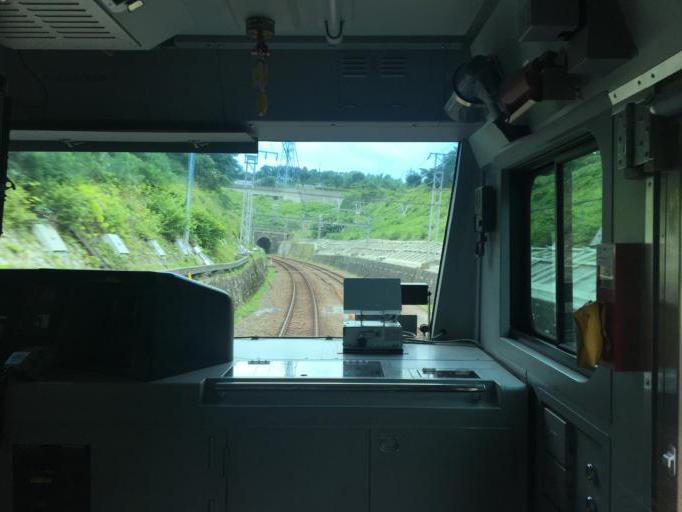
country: JP
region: Kanagawa
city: Yokohama
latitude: 35.4394
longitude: 139.5626
